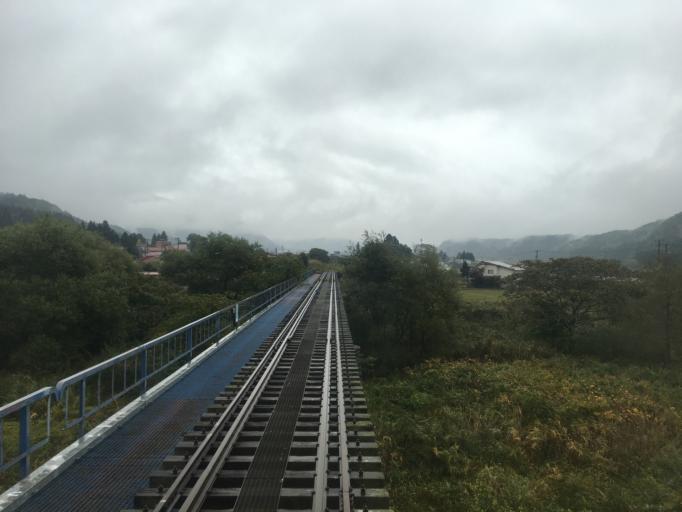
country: JP
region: Yamagata
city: Obanazawa
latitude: 38.7537
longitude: 140.5205
